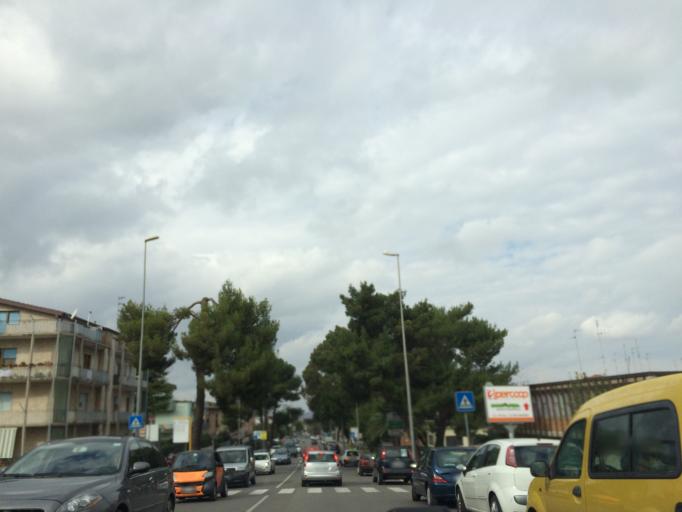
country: IT
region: Basilicate
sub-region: Provincia di Matera
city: Matera
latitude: 40.6714
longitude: 16.5956
